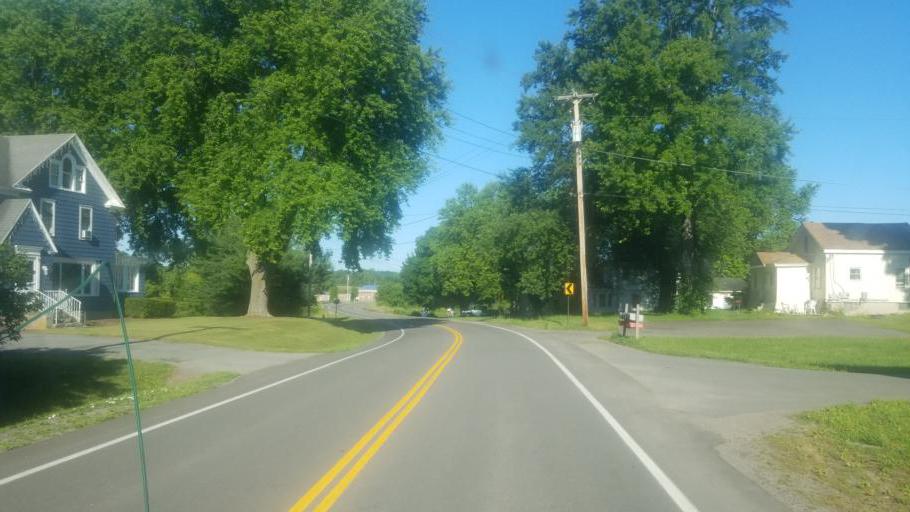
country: US
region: New York
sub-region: Wayne County
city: Newark
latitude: 43.0642
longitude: -77.0897
